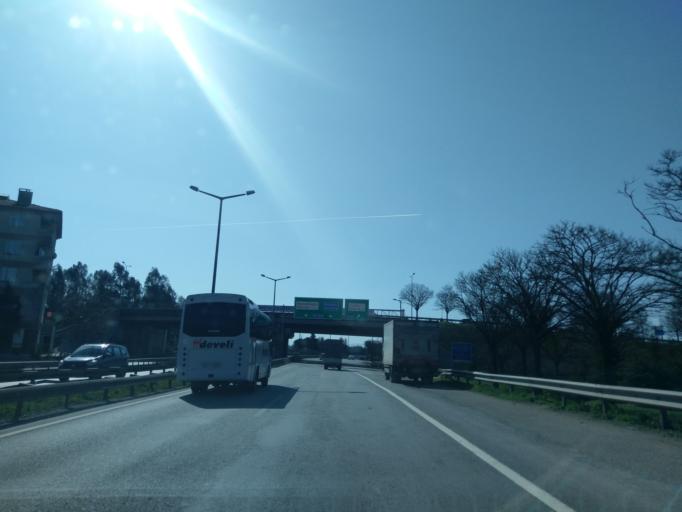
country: TR
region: Kocaeli
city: Darica
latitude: 40.8185
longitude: 29.3649
